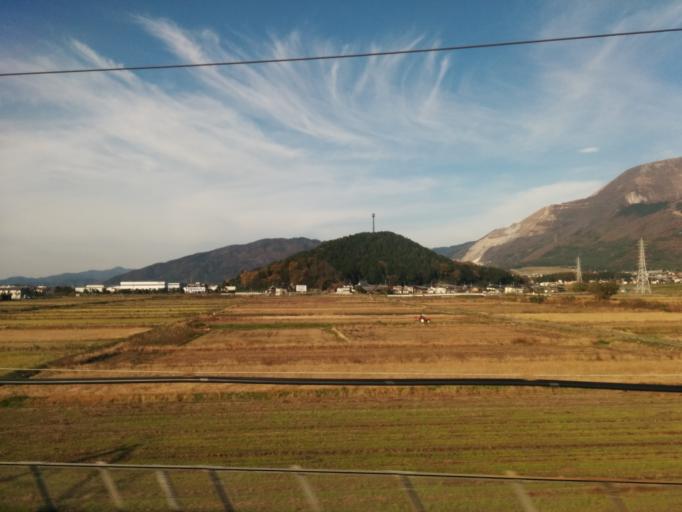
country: JP
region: Shiga Prefecture
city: Nagahama
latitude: 35.3672
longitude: 136.3722
